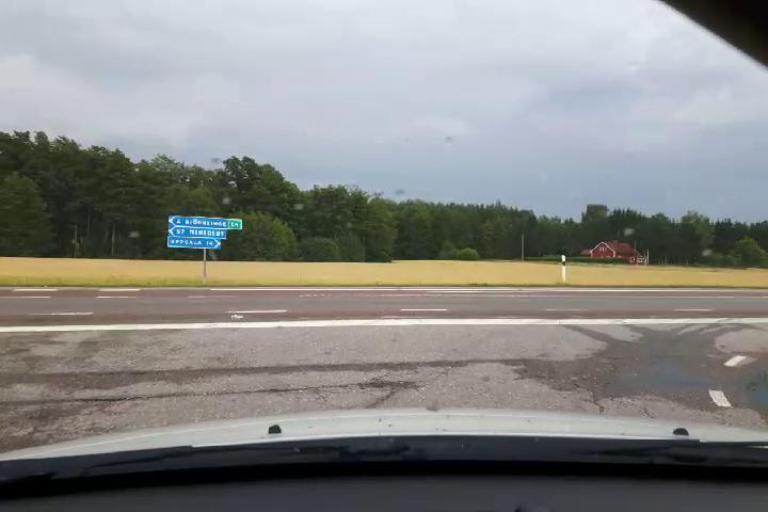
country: SE
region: Uppsala
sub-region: Osthammars Kommun
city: Bjorklinge
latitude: 59.9674
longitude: 17.5803
